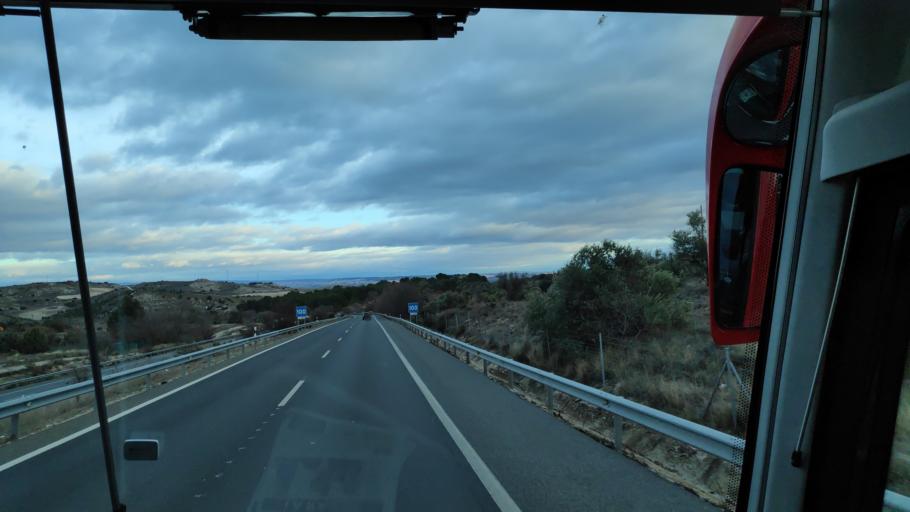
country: ES
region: Madrid
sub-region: Provincia de Madrid
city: Villarejo de Salvanes
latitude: 40.1490
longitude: -3.2307
